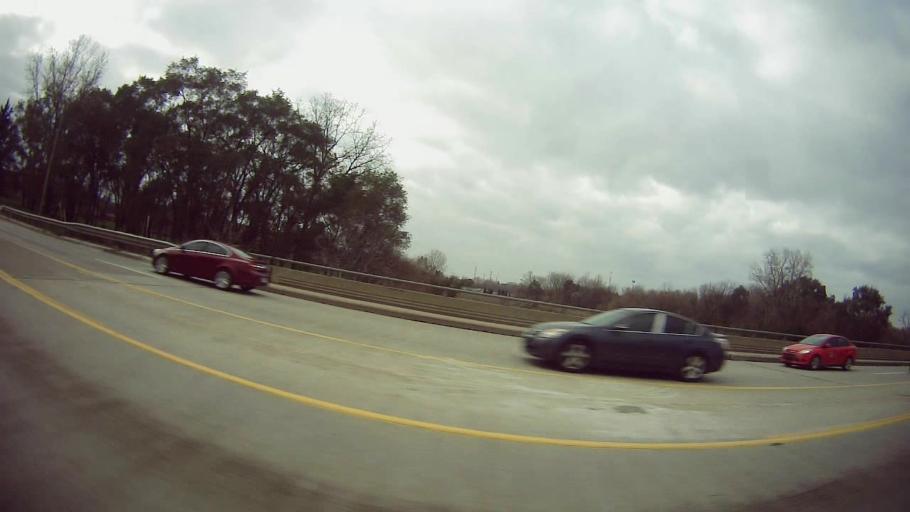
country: US
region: Michigan
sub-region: Macomb County
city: Fraser
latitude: 42.5493
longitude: -82.9895
